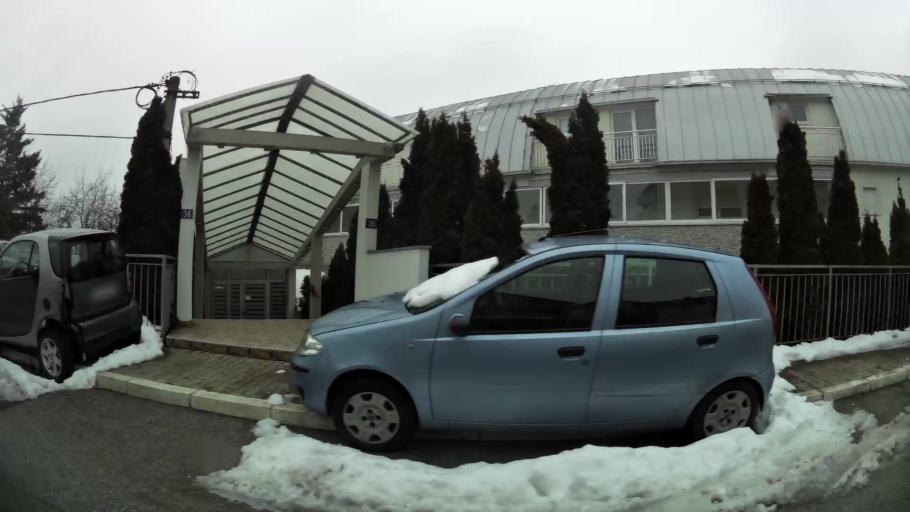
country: RS
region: Central Serbia
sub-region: Belgrade
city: Savski Venac
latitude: 44.7643
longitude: 20.4579
